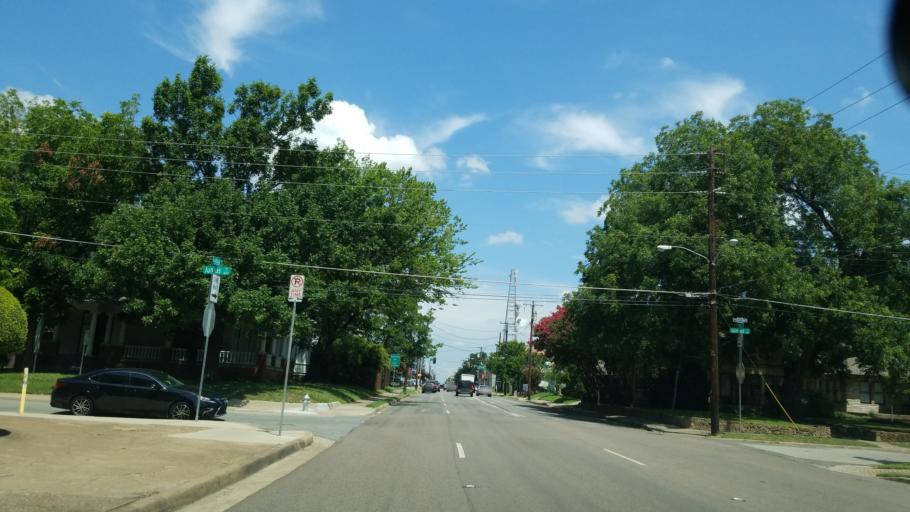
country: US
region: Texas
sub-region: Dallas County
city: Dallas
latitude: 32.7942
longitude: -96.7740
